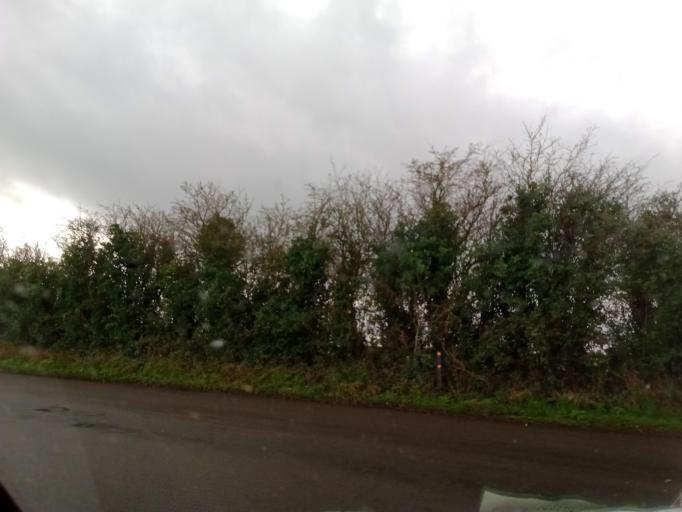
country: IE
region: Munster
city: Thurles
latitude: 52.6135
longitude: -7.7743
